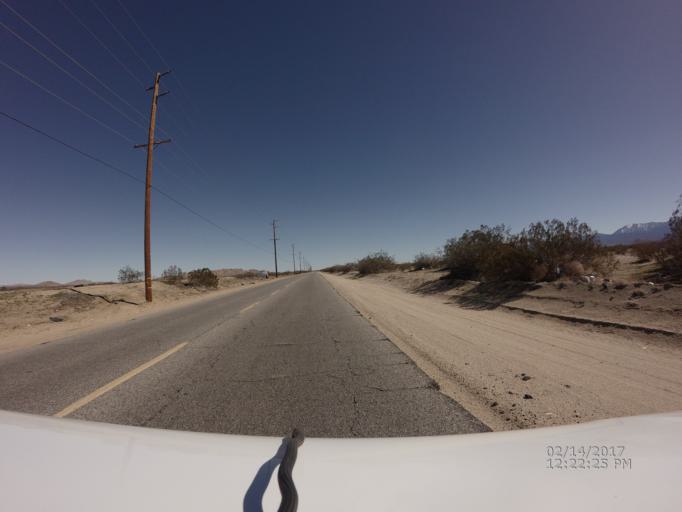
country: US
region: California
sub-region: Los Angeles County
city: Littlerock
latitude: 34.5799
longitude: -117.9260
